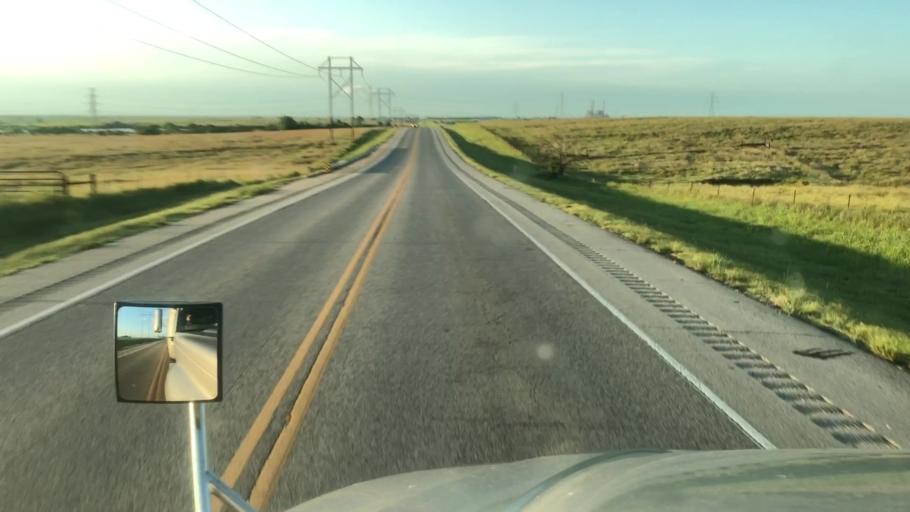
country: US
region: Oklahoma
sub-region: Noble County
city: Perry
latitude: 36.3937
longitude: -97.0676
